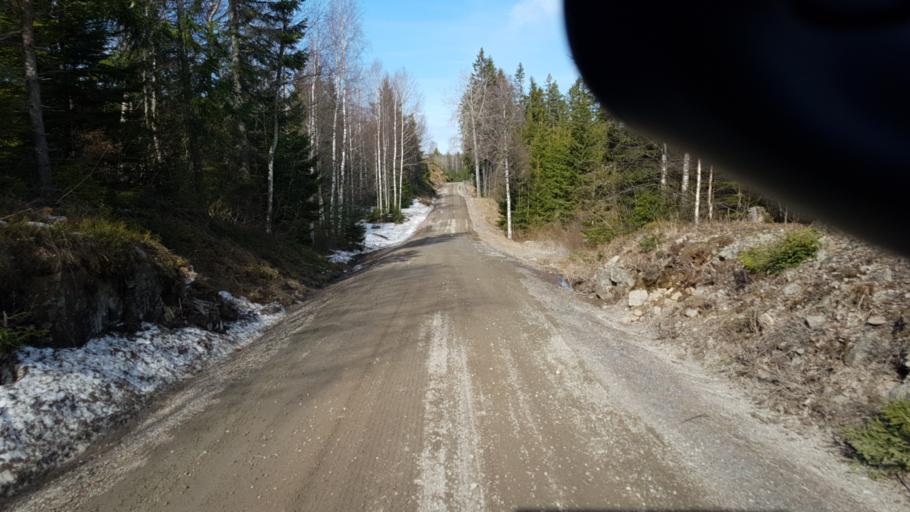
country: SE
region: Vaermland
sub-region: Arvika Kommun
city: Arvika
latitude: 59.5355
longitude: 12.4561
